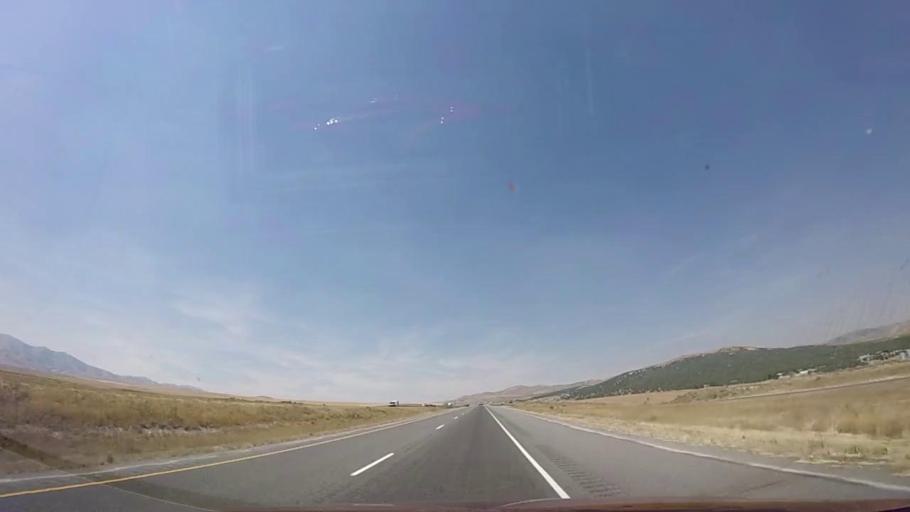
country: US
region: Idaho
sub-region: Power County
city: American Falls
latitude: 42.1499
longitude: -112.9836
